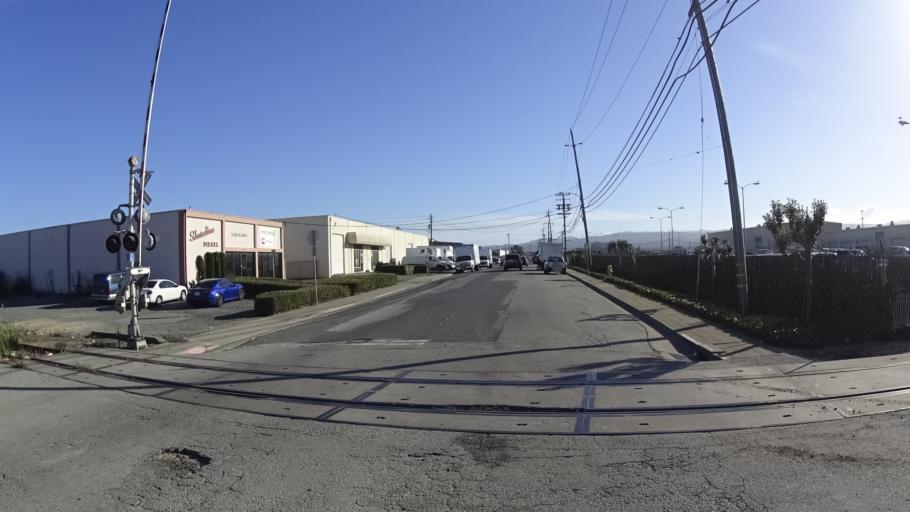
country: US
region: California
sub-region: San Mateo County
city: South San Francisco
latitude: 37.6517
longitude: -122.4002
